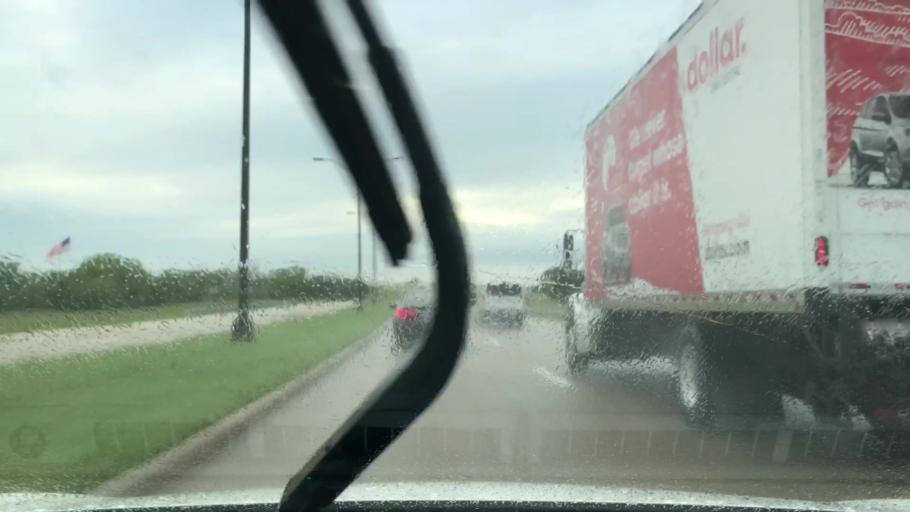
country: US
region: Texas
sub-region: Dallas County
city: Coppell
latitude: 32.9257
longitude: -97.0326
